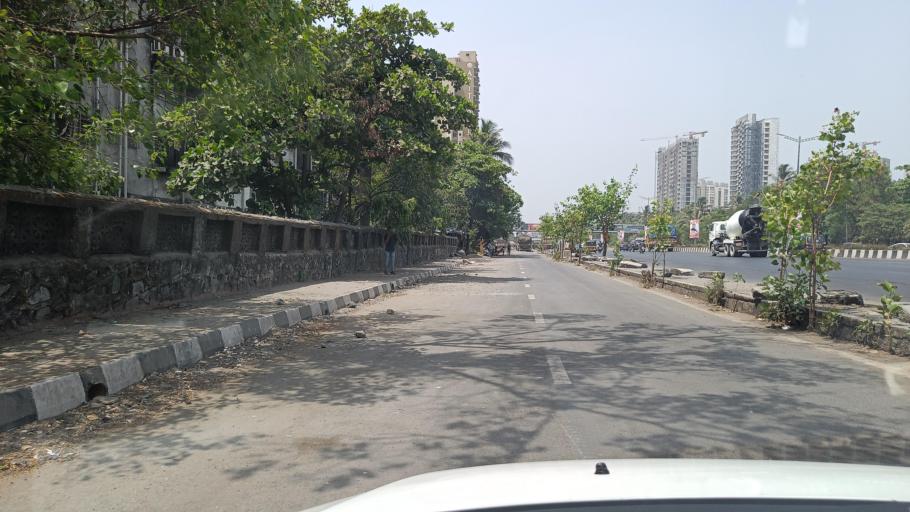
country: IN
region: Maharashtra
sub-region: Mumbai Suburban
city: Powai
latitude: 19.1166
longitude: 72.9352
